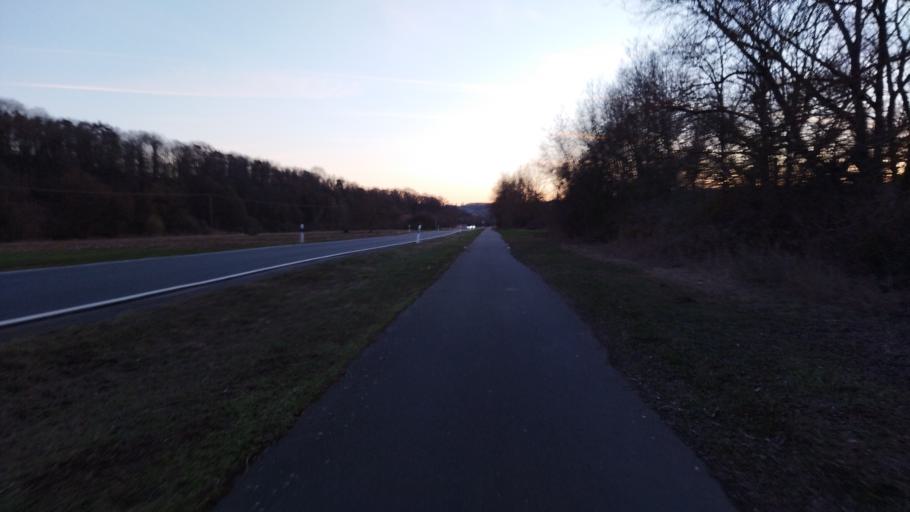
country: DE
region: Bavaria
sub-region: Regierungsbezirk Unterfranken
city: Nordheim
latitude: 49.8853
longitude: 10.1786
